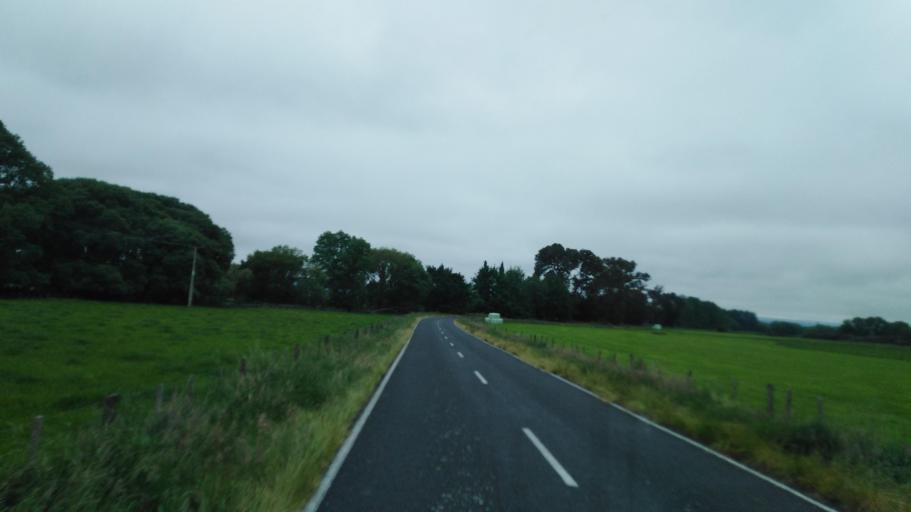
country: NZ
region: Bay of Plenty
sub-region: Rotorua District
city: Rotorua
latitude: -38.4073
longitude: 176.3333
